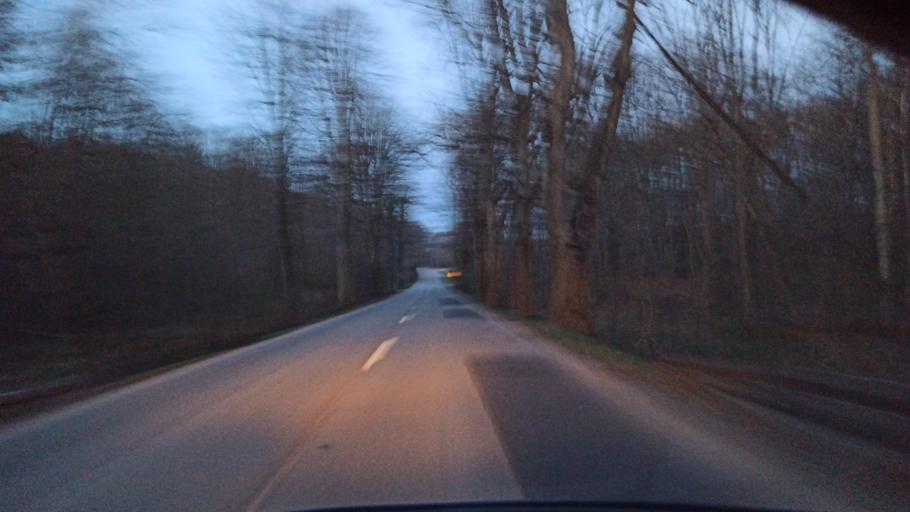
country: PL
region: Warmian-Masurian Voivodeship
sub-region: Powiat elblaski
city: Gronowo Gorne
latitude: 54.1852
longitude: 19.4588
